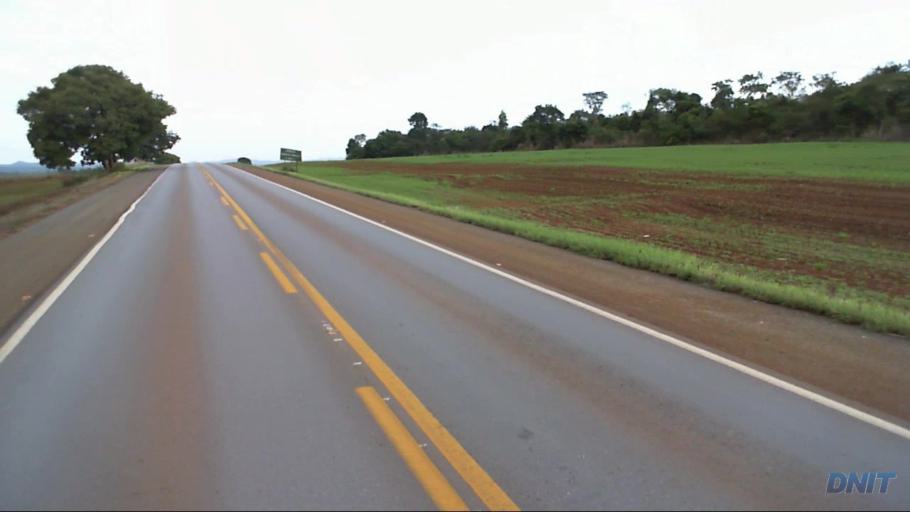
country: BR
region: Goias
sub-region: Uruacu
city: Uruacu
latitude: -14.6634
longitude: -49.1517
